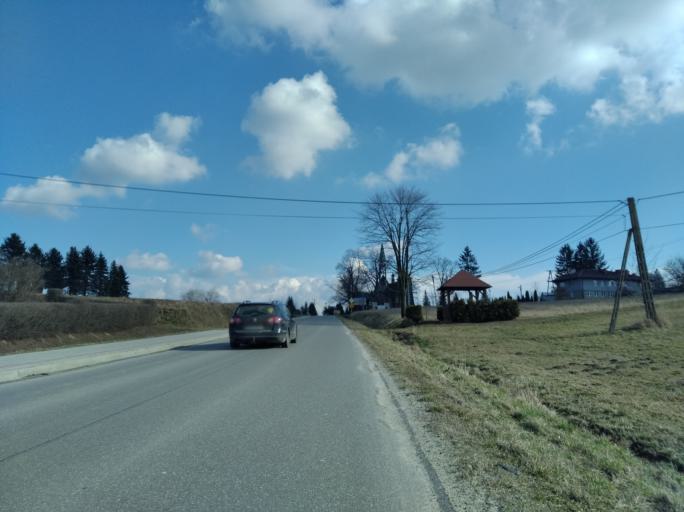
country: PL
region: Subcarpathian Voivodeship
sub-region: Powiat strzyzowski
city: Frysztak
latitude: 49.8485
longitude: 21.5244
